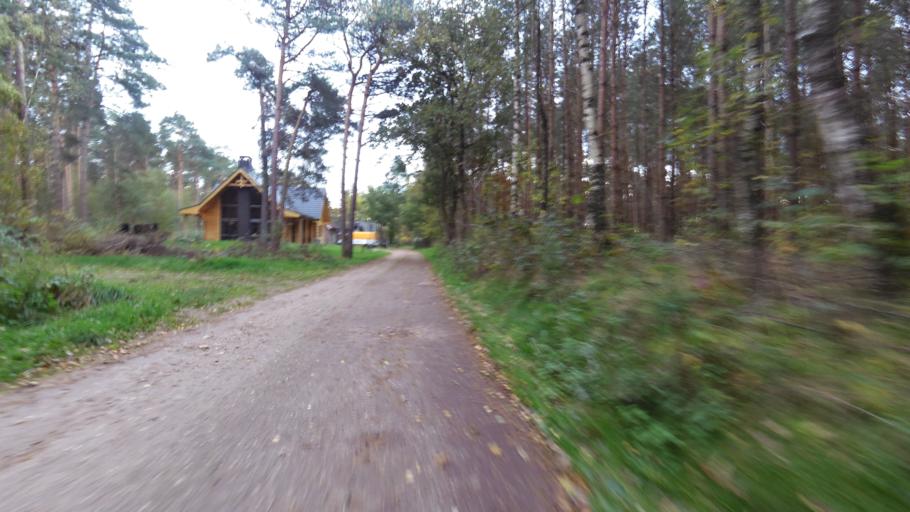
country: NL
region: Gelderland
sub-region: Gemeente Oldebroek
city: Oldebroek
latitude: 52.4339
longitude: 5.9390
